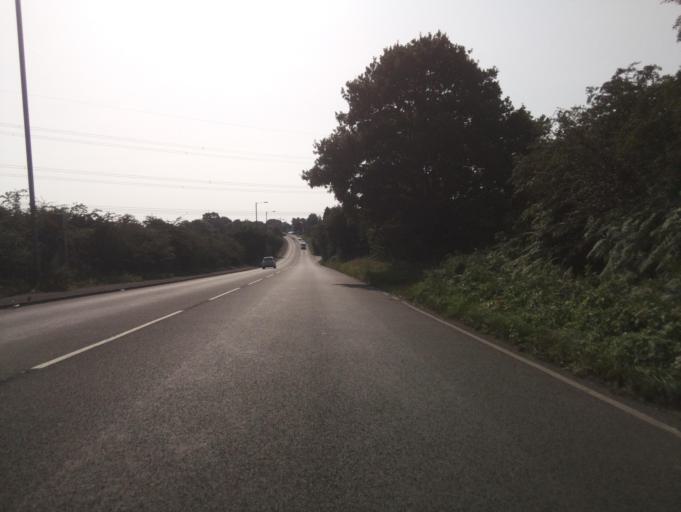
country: GB
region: England
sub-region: Walsall
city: Aldridge
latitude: 52.6191
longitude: -1.8904
